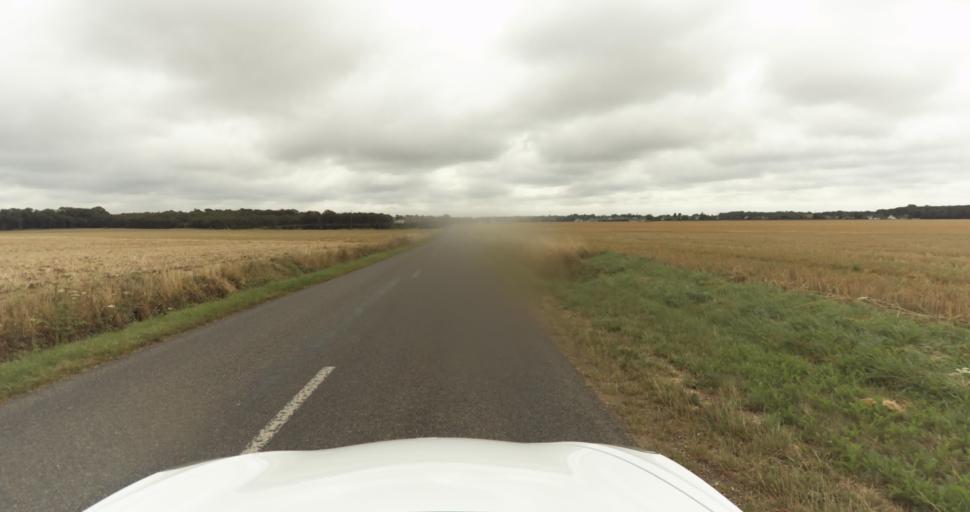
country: FR
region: Haute-Normandie
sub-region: Departement de l'Eure
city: Aviron
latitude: 49.0621
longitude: 1.0758
